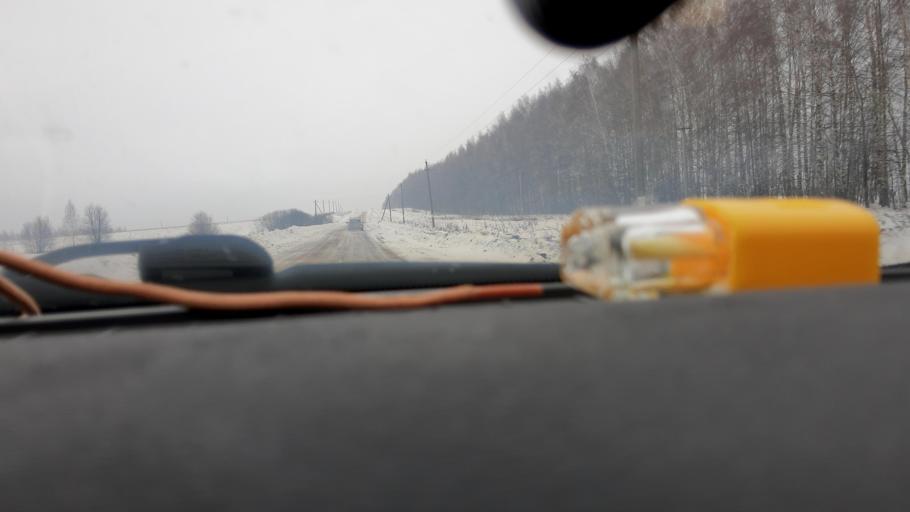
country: RU
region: Bashkortostan
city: Ulukulevo
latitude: 54.5719
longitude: 56.4295
